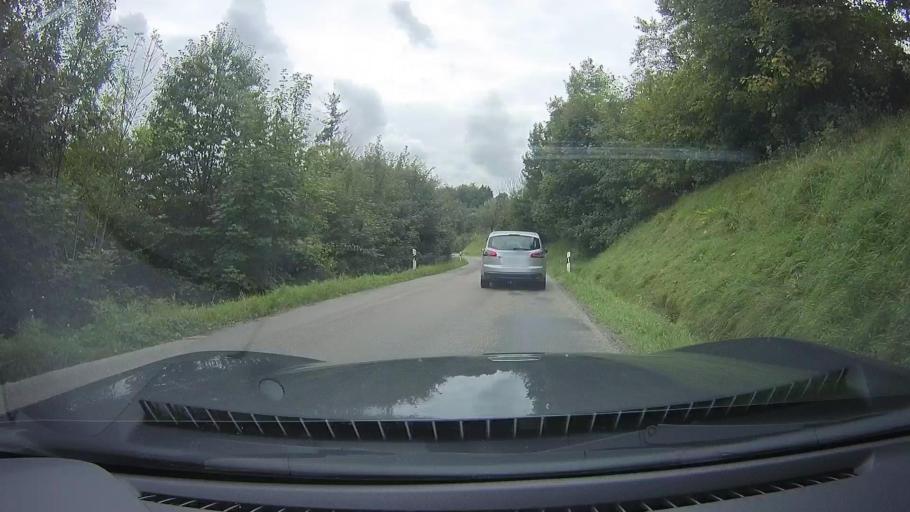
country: DE
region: Baden-Wuerttemberg
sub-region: Regierungsbezirk Stuttgart
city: Murrhardt
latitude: 49.0005
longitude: 9.5696
